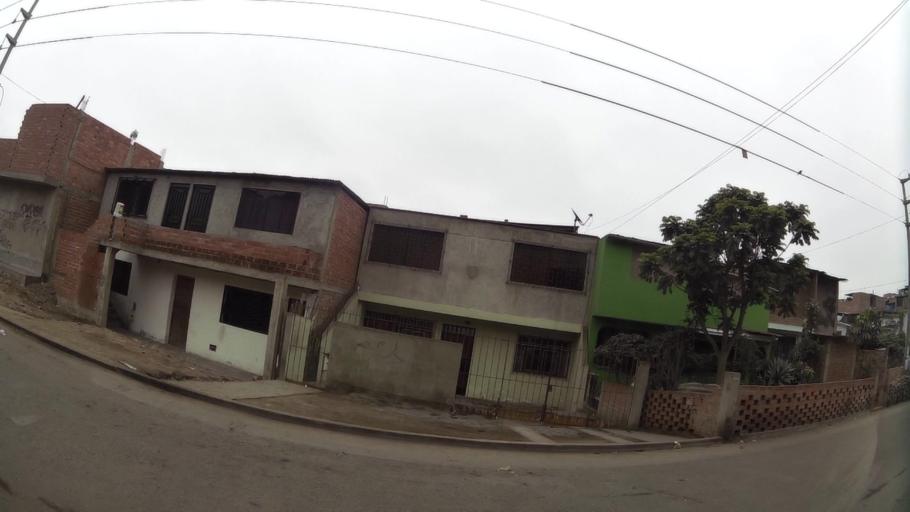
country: PE
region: Lima
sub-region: Lima
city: Surco
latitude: -12.1740
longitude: -76.9559
